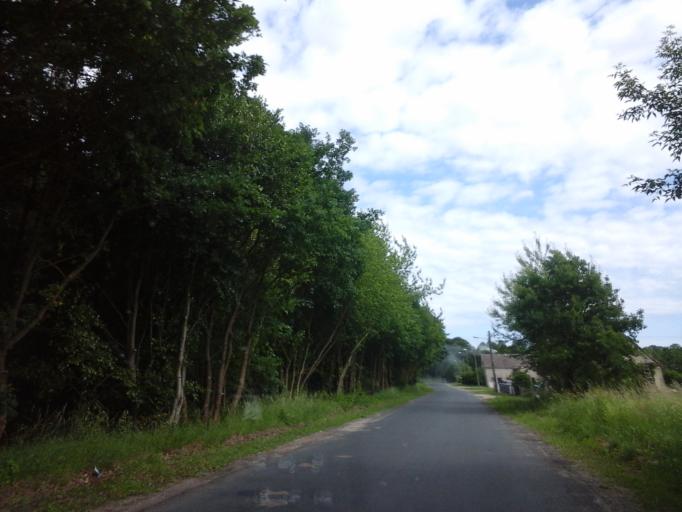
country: PL
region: West Pomeranian Voivodeship
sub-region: Powiat choszczenski
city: Recz
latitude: 53.2469
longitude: 15.5422
